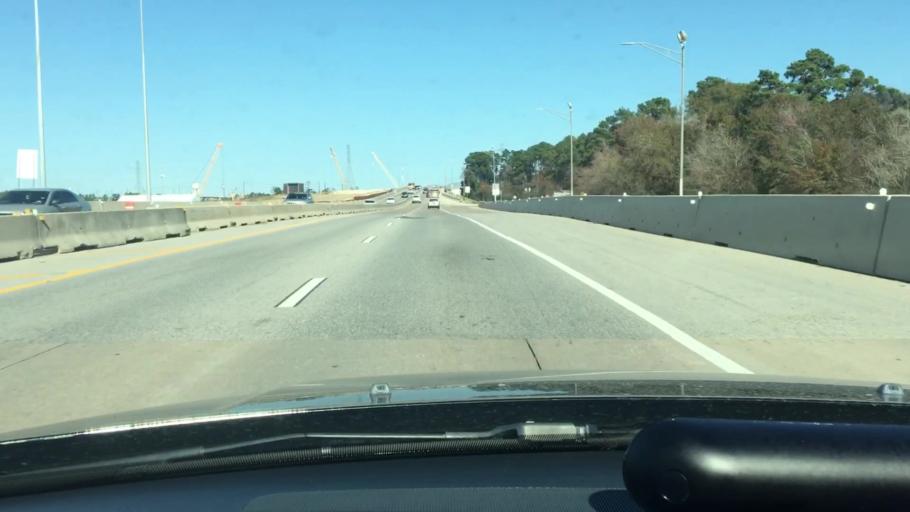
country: US
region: Texas
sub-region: Harris County
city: Cloverleaf
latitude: 29.7502
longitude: -95.1457
